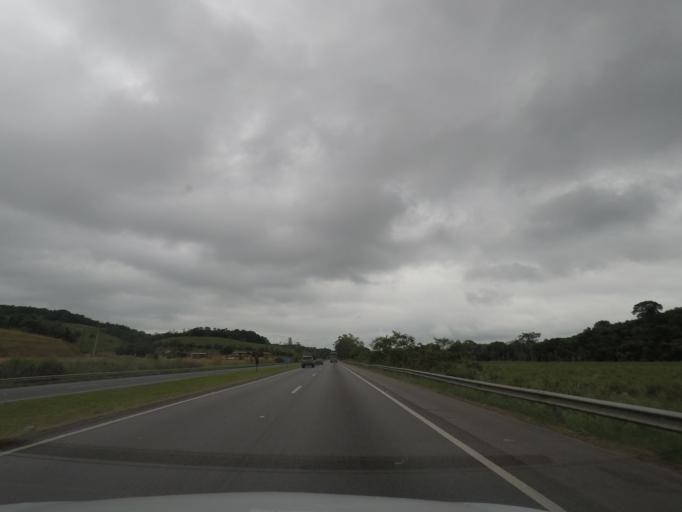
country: BR
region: Sao Paulo
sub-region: Registro
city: Registro
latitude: -24.4152
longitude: -47.7599
